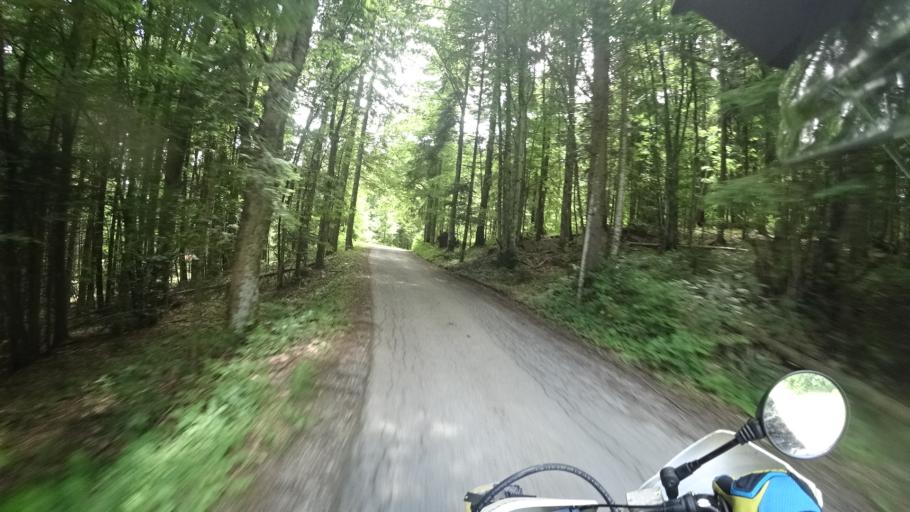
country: SI
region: Loska Dolina
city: Leskova Dolina
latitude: 45.6040
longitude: 14.5564
